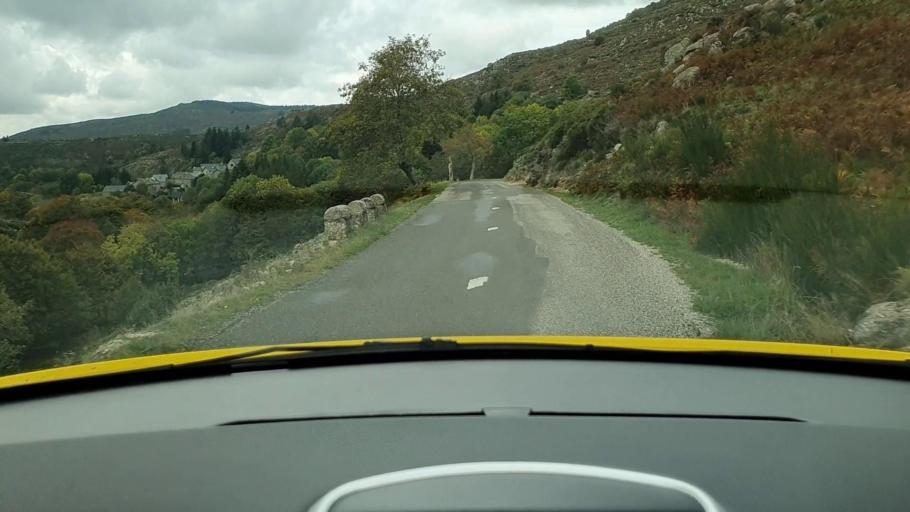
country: FR
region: Languedoc-Roussillon
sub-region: Departement de la Lozere
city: Meyrueis
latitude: 44.0754
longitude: 3.4938
